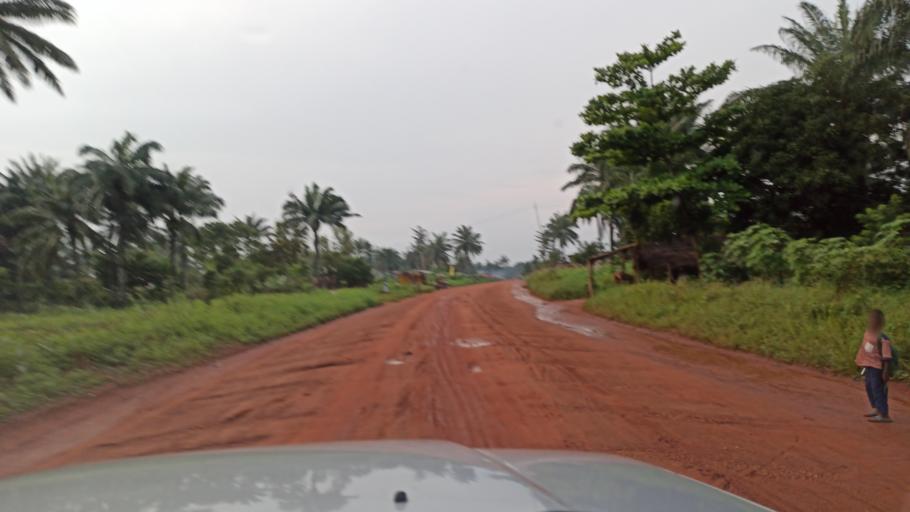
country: BJ
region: Queme
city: Porto-Novo
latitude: 6.5495
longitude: 2.6101
